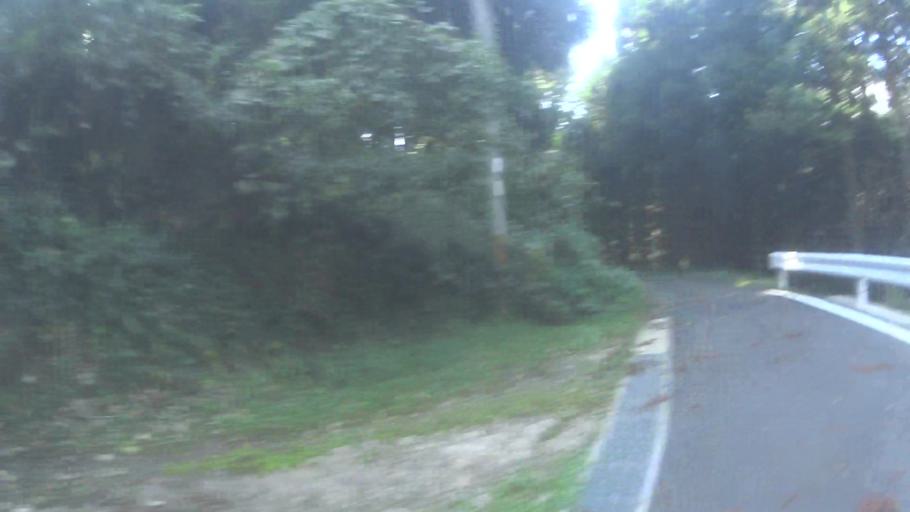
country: JP
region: Kyoto
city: Miyazu
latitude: 35.7139
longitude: 135.1668
